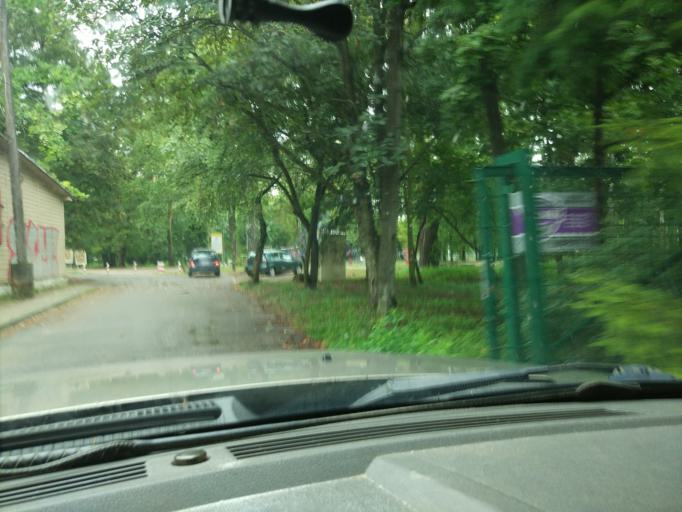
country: PL
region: Masovian Voivodeship
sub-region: Powiat grodziski
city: Podkowa Lesna
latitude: 52.1218
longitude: 20.7248
